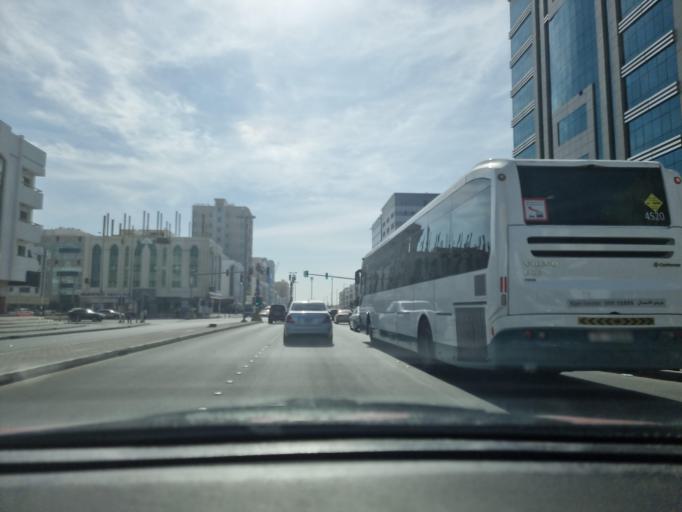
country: AE
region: Abu Dhabi
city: Abu Dhabi
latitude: 24.3254
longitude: 54.5352
